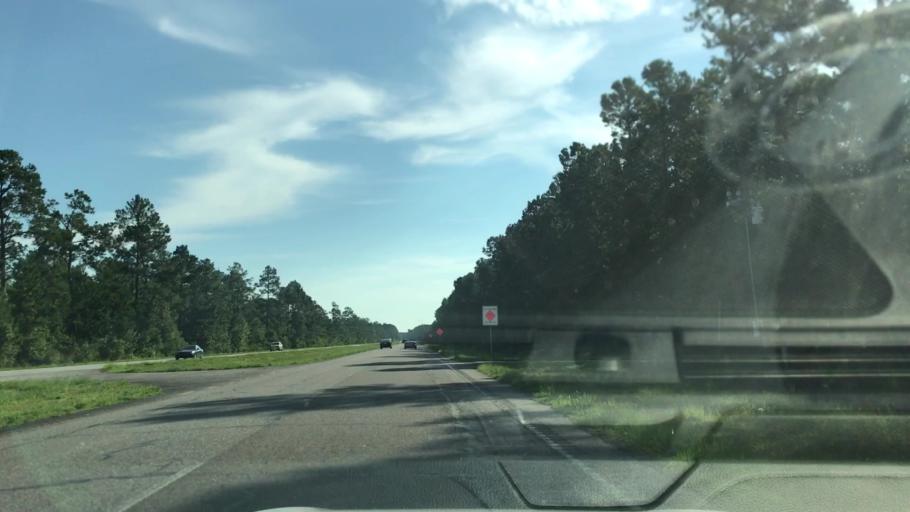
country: US
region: South Carolina
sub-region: Charleston County
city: Awendaw
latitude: 33.0819
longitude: -79.4991
